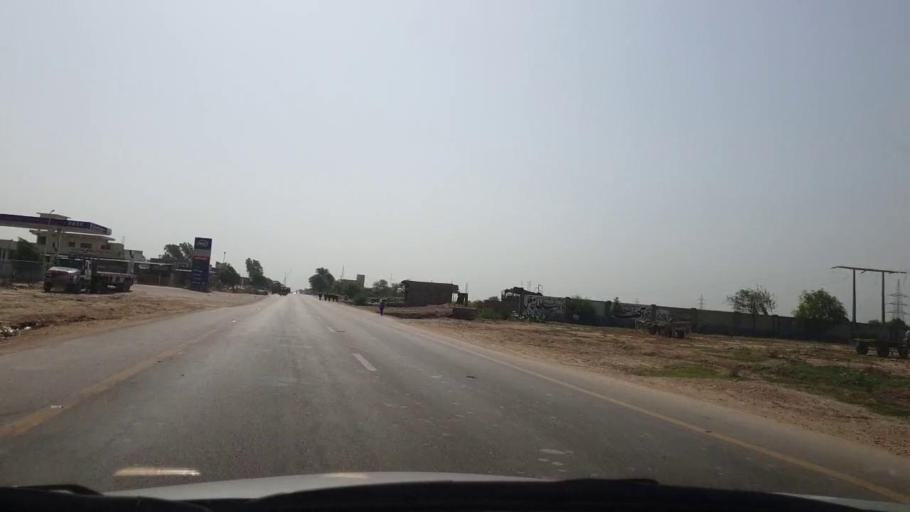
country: PK
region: Sindh
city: Tando Muhammad Khan
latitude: 25.1039
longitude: 68.5870
